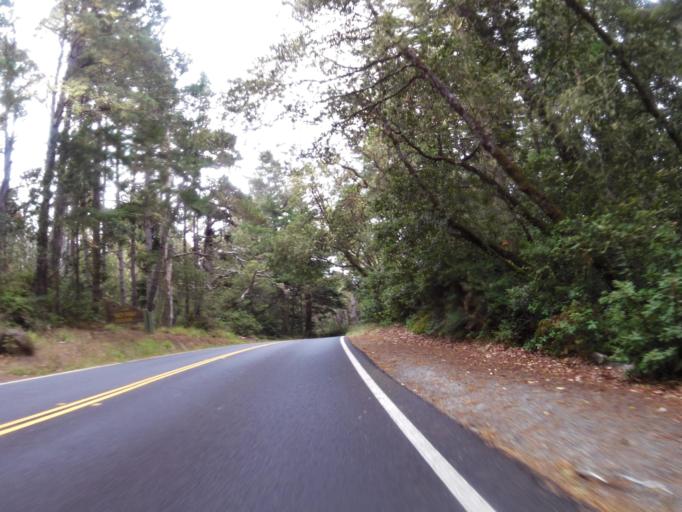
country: US
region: California
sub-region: Sonoma County
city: Sea Ranch
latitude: 38.5591
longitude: -123.3103
